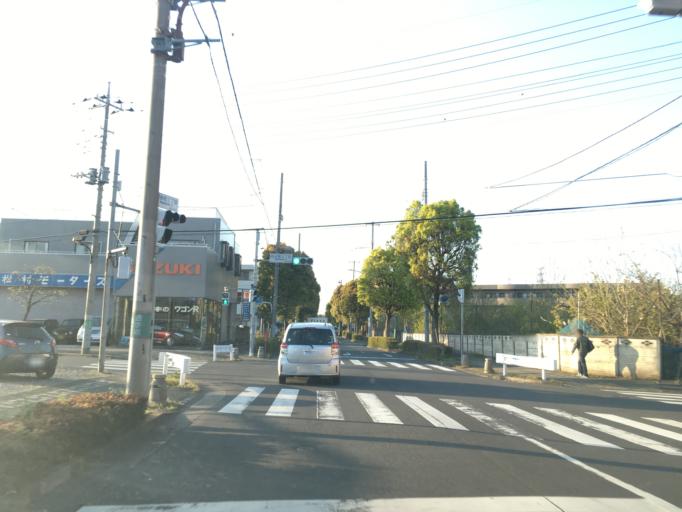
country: JP
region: Tokyo
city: Kokubunji
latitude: 35.6686
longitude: 139.4504
